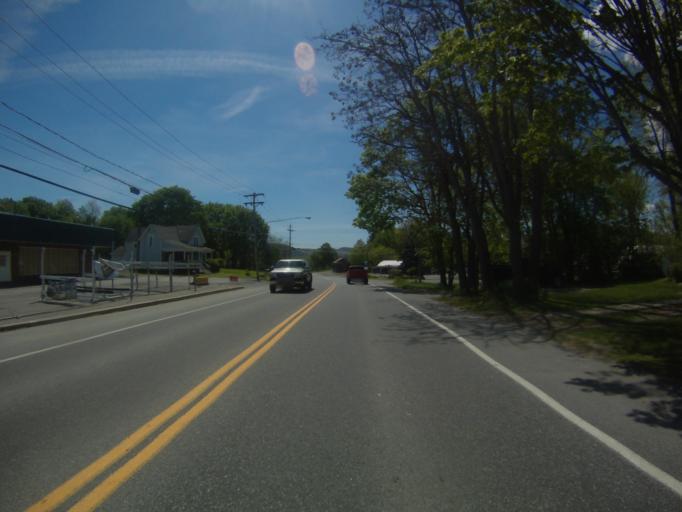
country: US
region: New York
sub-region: Essex County
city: Ticonderoga
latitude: 43.8536
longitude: -73.4378
